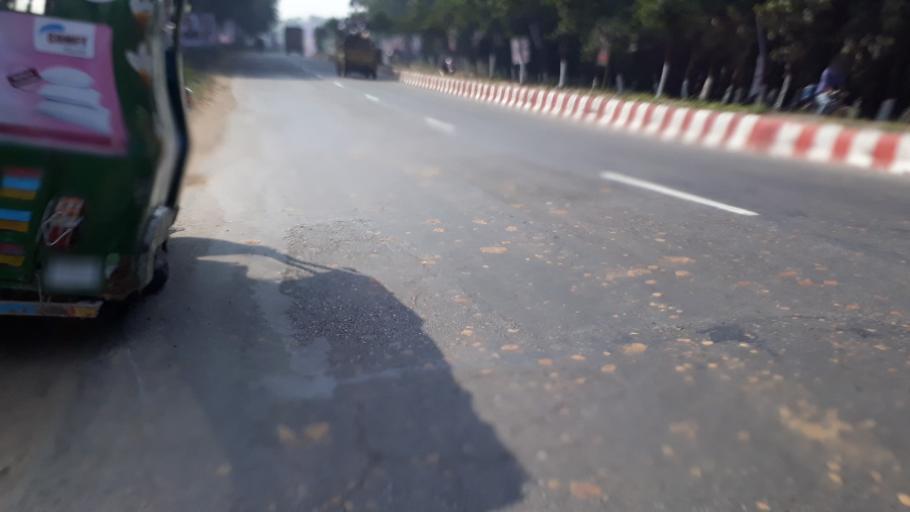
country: BD
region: Dhaka
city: Tungi
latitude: 23.8700
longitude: 90.2728
